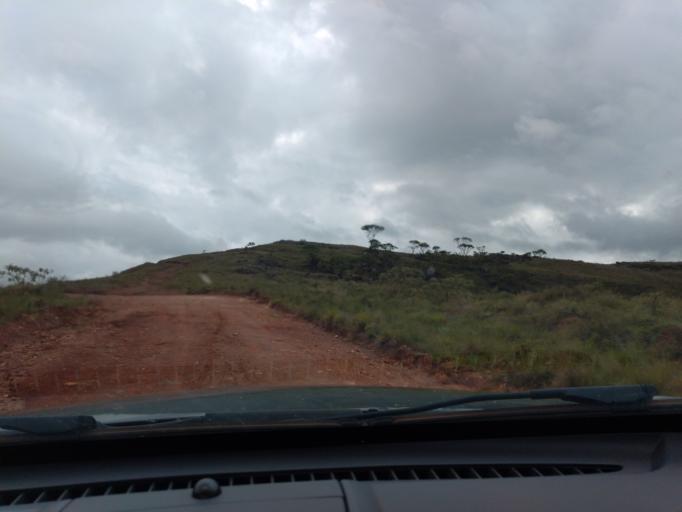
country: BR
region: Minas Gerais
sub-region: Lavras
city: Lavras
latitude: -21.5164
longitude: -44.9301
